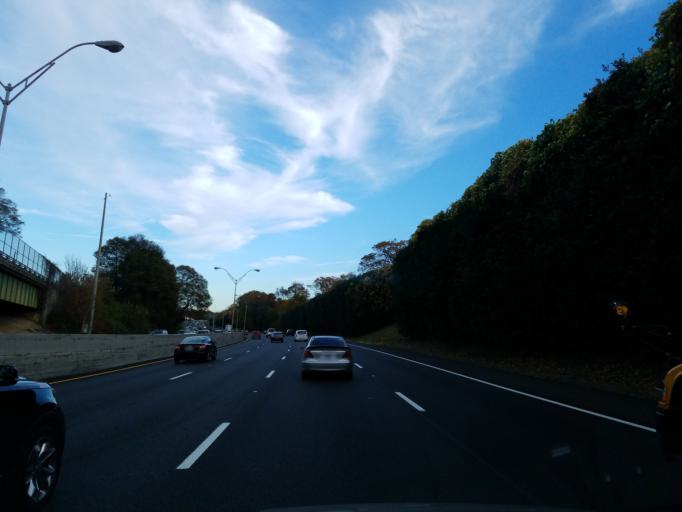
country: US
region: Georgia
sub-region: Fulton County
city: Atlanta
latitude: 33.7473
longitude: -84.4387
